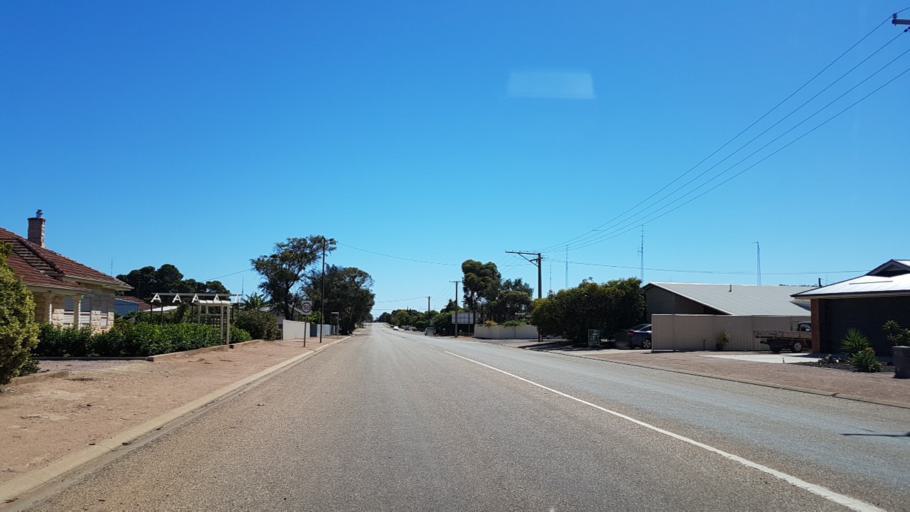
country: AU
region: South Australia
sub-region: Copper Coast
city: Kadina
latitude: -33.9665
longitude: 137.7226
